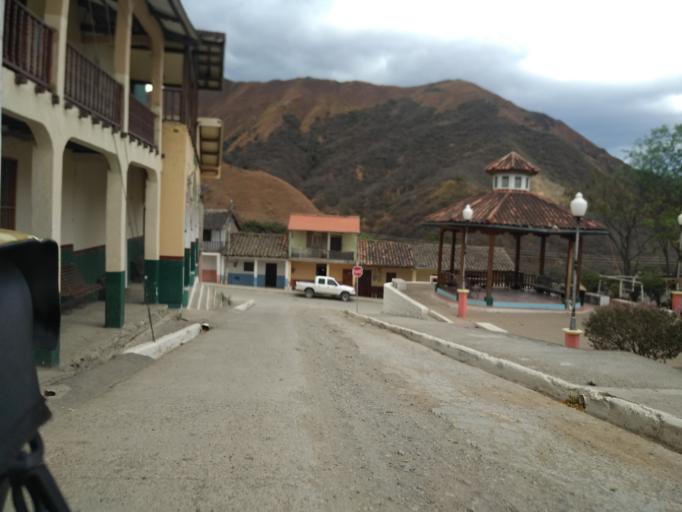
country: EC
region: Loja
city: Loja
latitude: -4.2434
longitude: -79.2213
